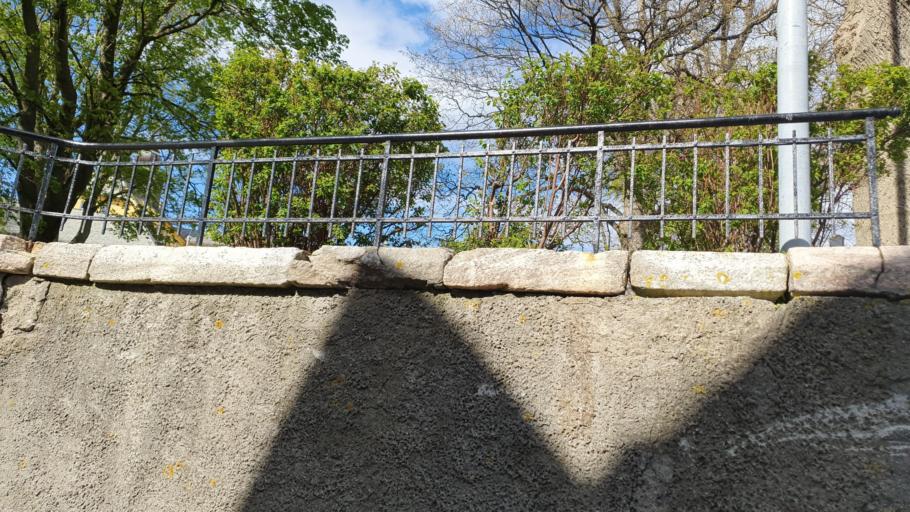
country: NO
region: More og Romsdal
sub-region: Alesund
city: Alesund
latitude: 62.4713
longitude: 6.1462
